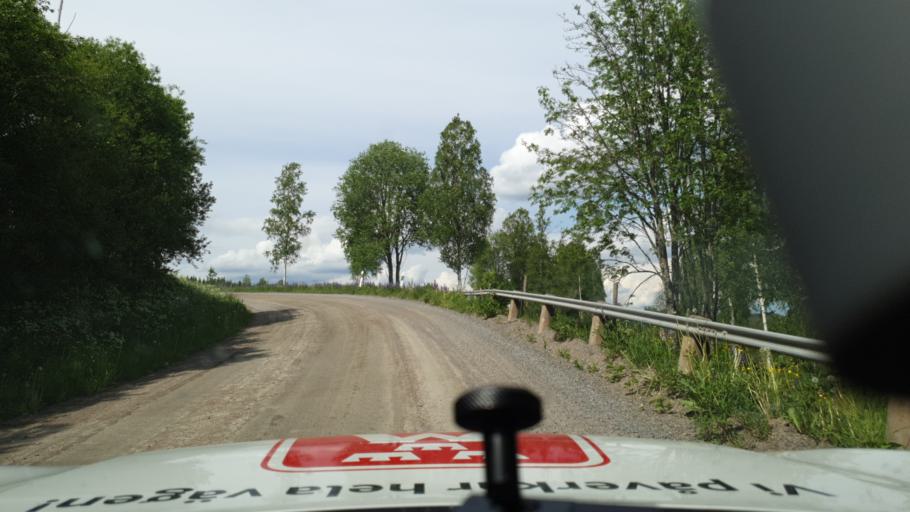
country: SE
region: Vaermland
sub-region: Torsby Kommun
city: Torsby
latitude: 59.9479
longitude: 12.9000
